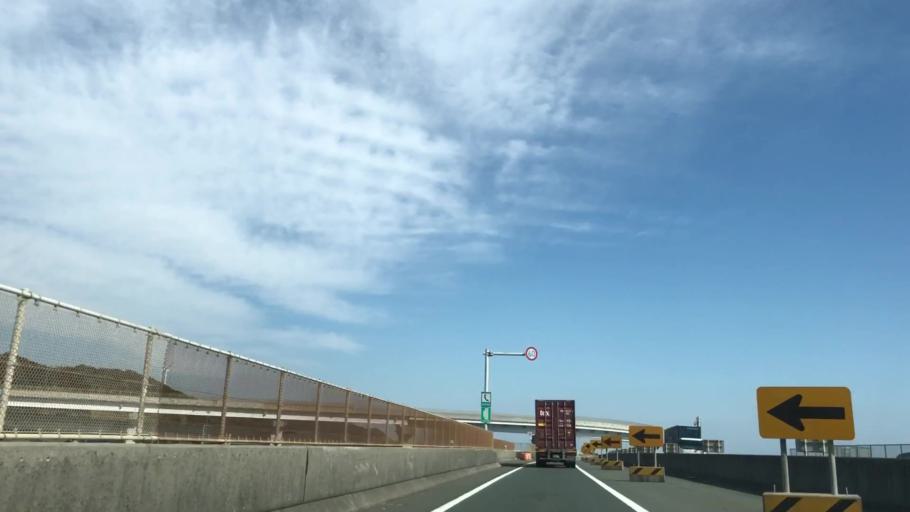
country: JP
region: Shizuoka
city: Kosai-shi
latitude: 34.6779
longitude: 137.5105
